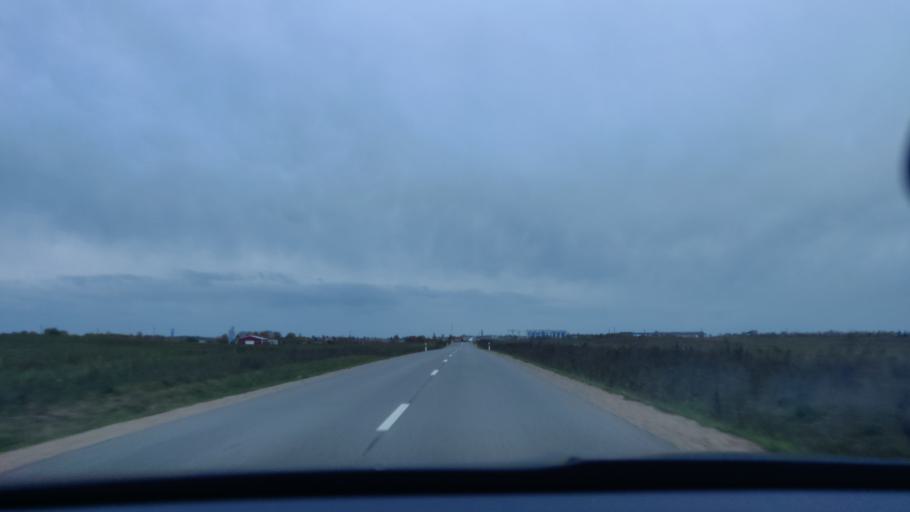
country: LT
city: Lentvaris
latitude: 54.6048
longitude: 25.0010
